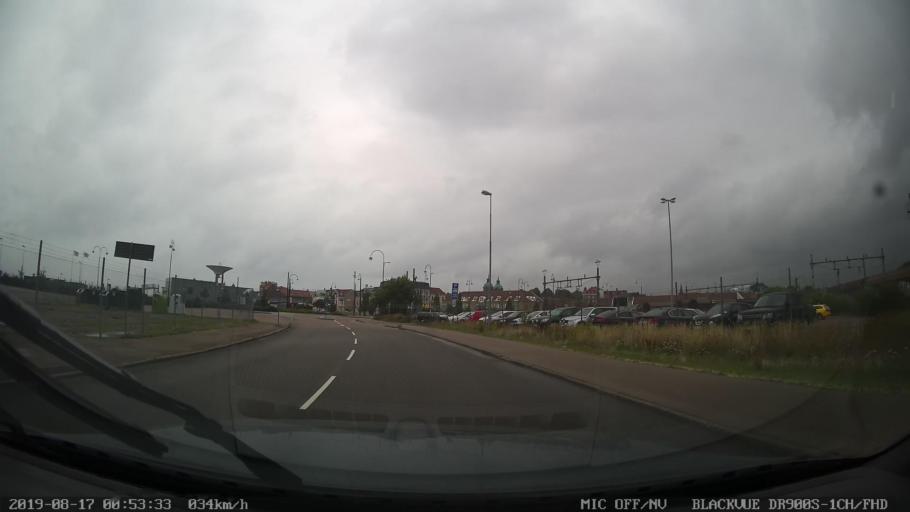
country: SE
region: Skane
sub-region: Landskrona
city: Landskrona
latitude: 55.8646
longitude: 12.8279
